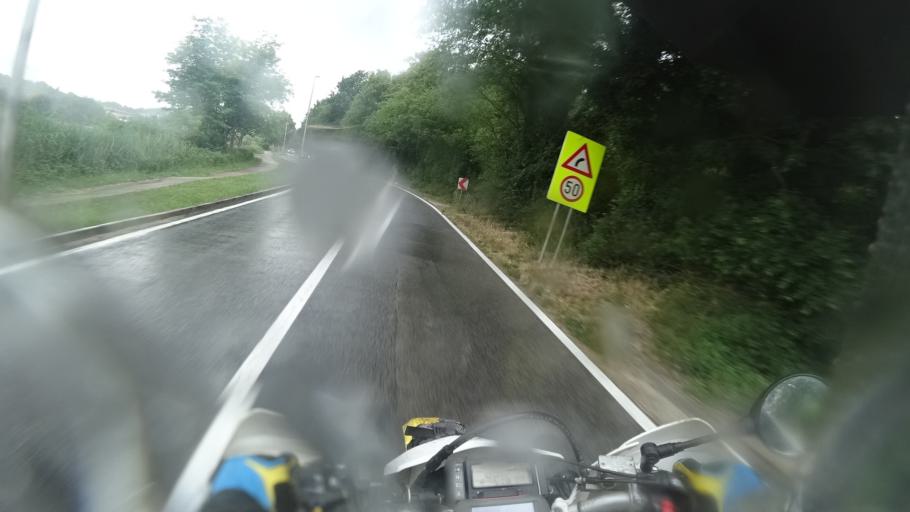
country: HR
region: Sibensko-Kniniska
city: Knin
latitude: 44.0412
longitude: 16.2084
